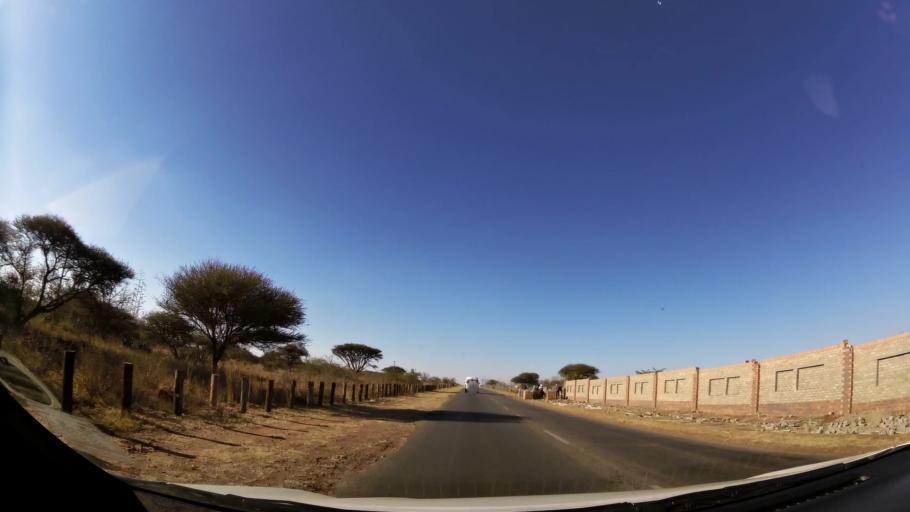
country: ZA
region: Limpopo
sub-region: Capricorn District Municipality
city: Polokwane
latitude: -23.8780
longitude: 29.4758
